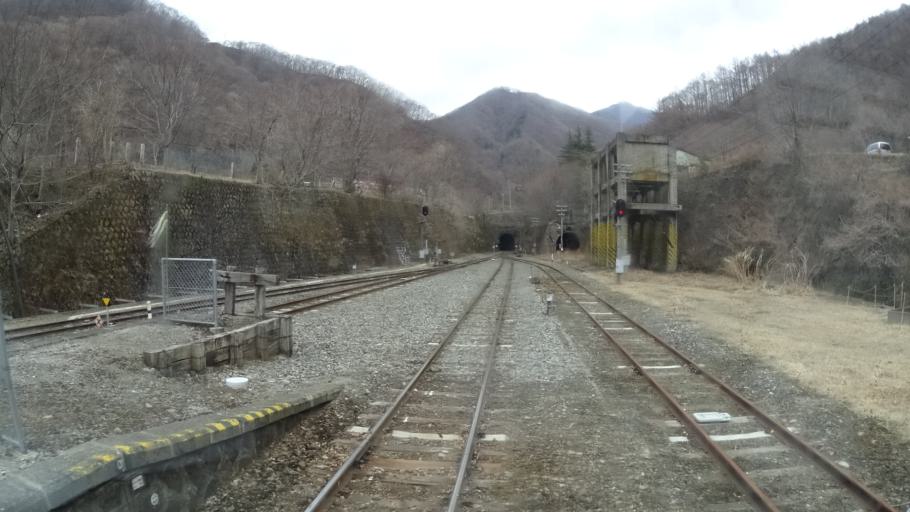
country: JP
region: Iwate
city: Kamaishi
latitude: 39.2811
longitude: 141.7181
